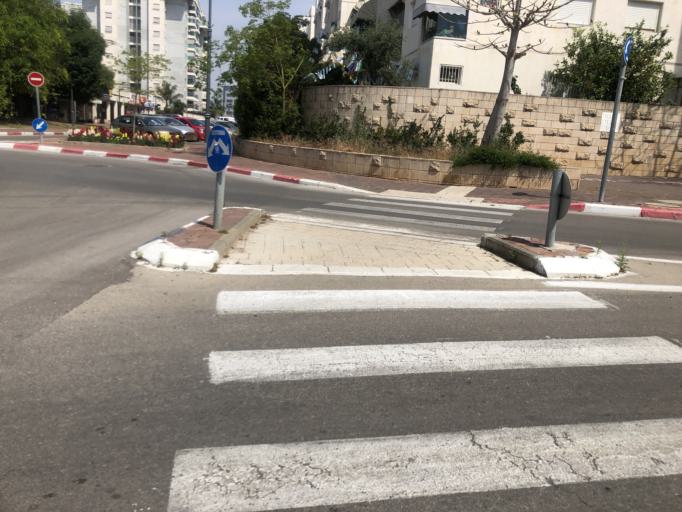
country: IL
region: Central District
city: Rosh Ha'Ayin
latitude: 32.0968
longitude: 34.9389
